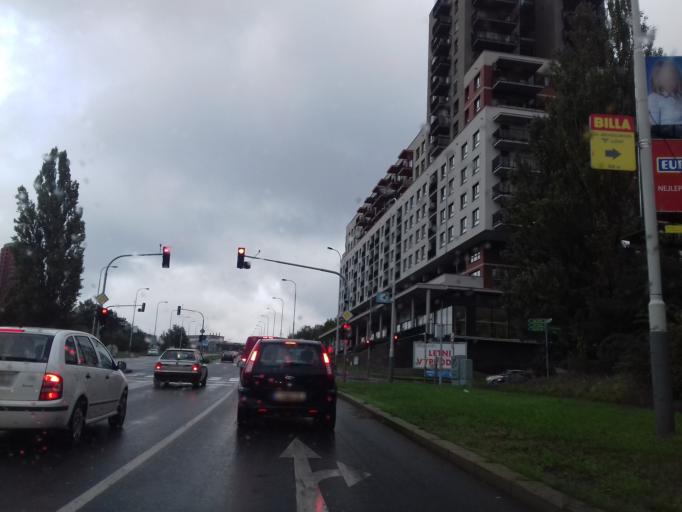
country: CZ
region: Praha
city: Branik
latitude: 50.0446
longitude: 14.3382
